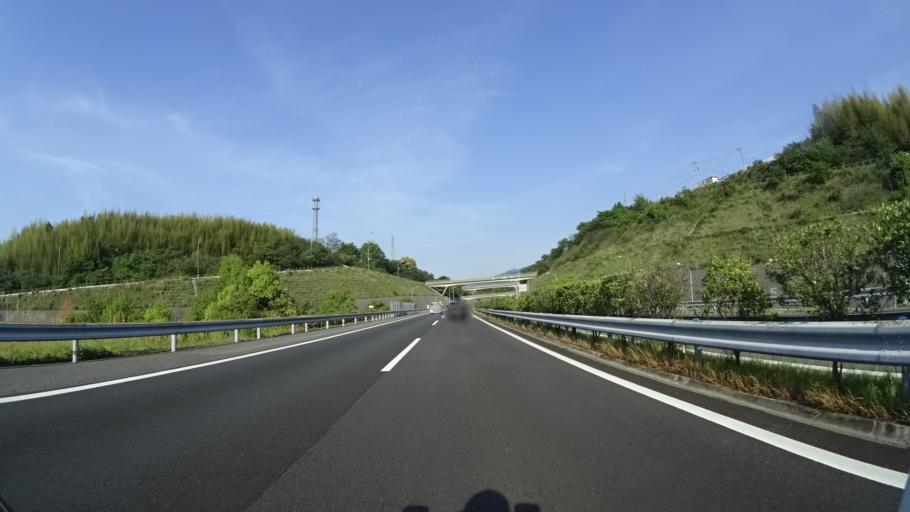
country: JP
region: Ehime
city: Saijo
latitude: 33.9121
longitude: 133.2374
